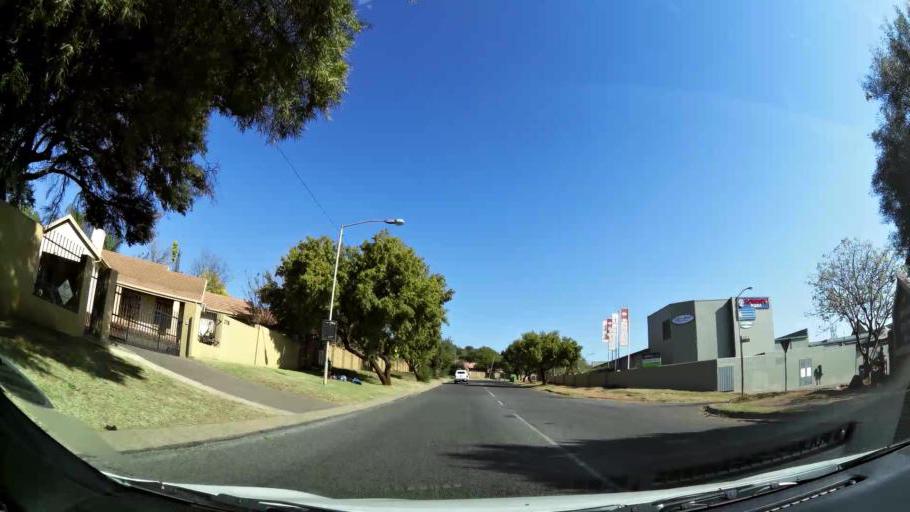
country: ZA
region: Gauteng
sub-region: City of Tshwane Metropolitan Municipality
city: Pretoria
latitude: -25.7943
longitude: 28.2710
